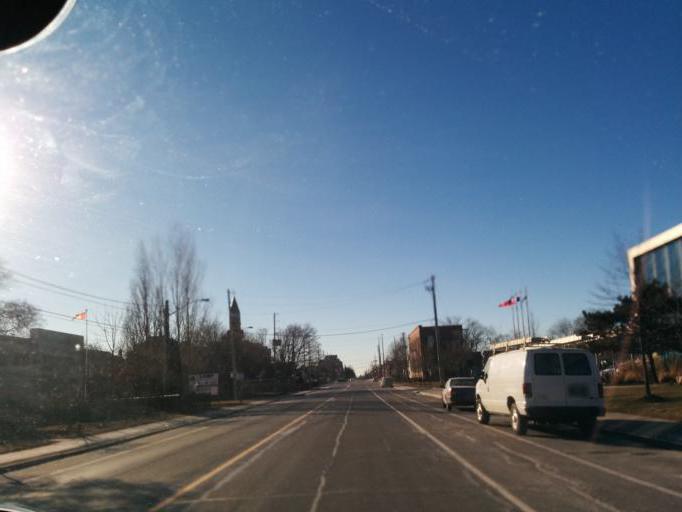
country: CA
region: Ontario
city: Etobicoke
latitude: 43.6040
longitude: -79.5032
